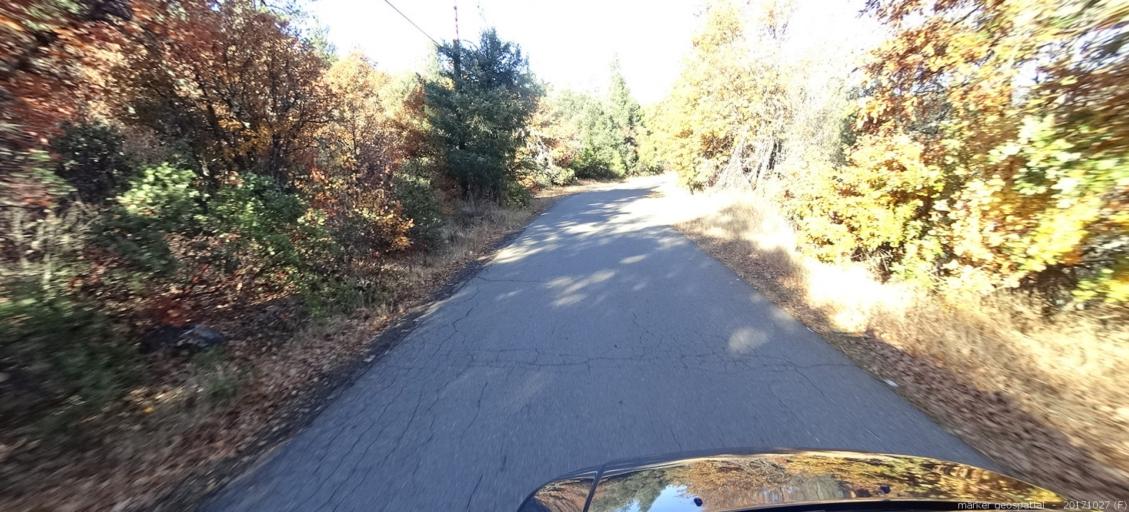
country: US
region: California
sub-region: Shasta County
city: Burney
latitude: 41.0200
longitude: -121.9133
